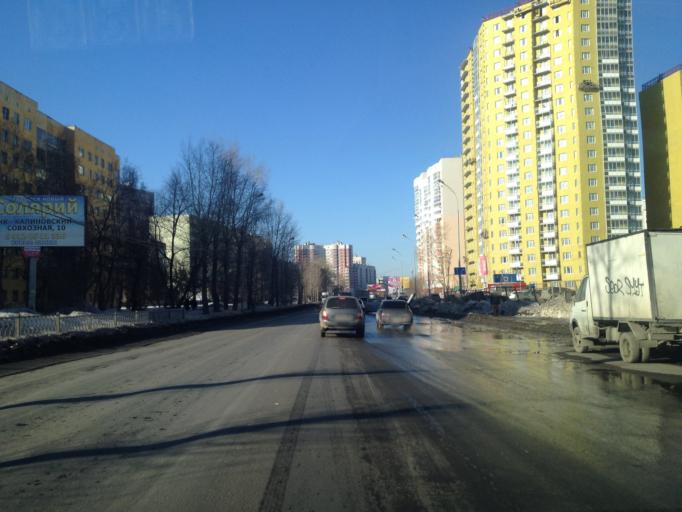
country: RU
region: Sverdlovsk
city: Yekaterinburg
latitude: 56.9045
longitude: 60.6226
